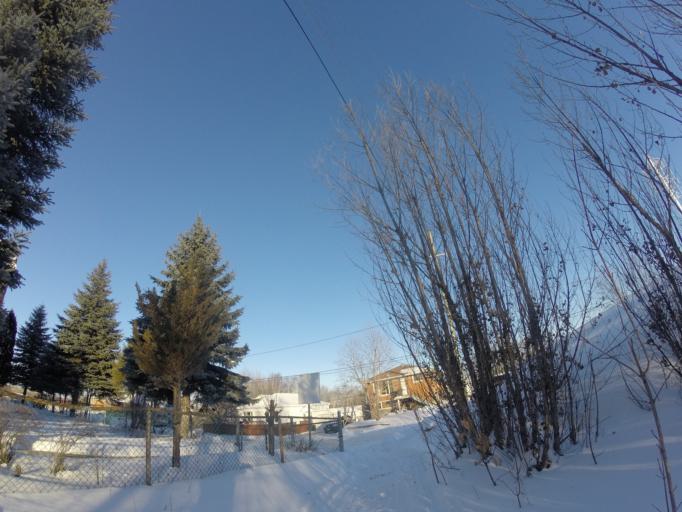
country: CA
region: Ontario
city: Greater Sudbury
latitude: 46.5042
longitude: -81.0022
